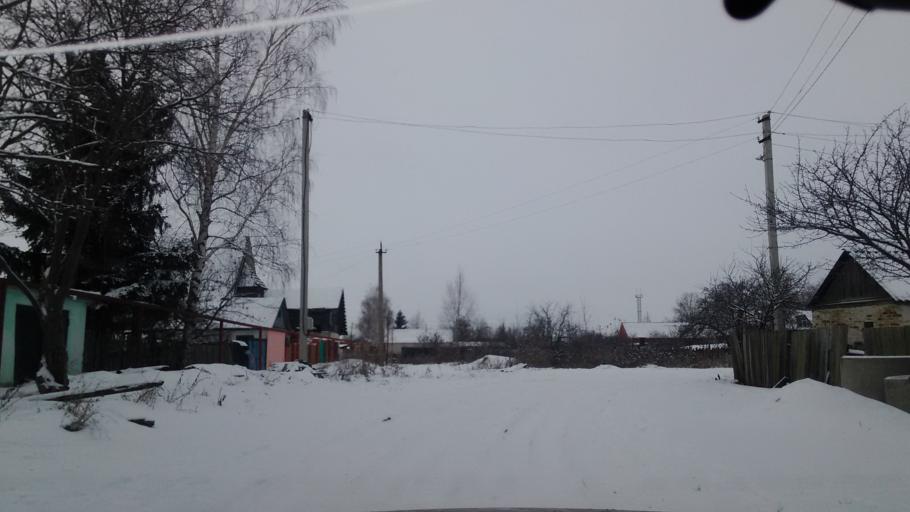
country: RU
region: Tula
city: Bogoroditsk
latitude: 53.7574
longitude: 38.1132
